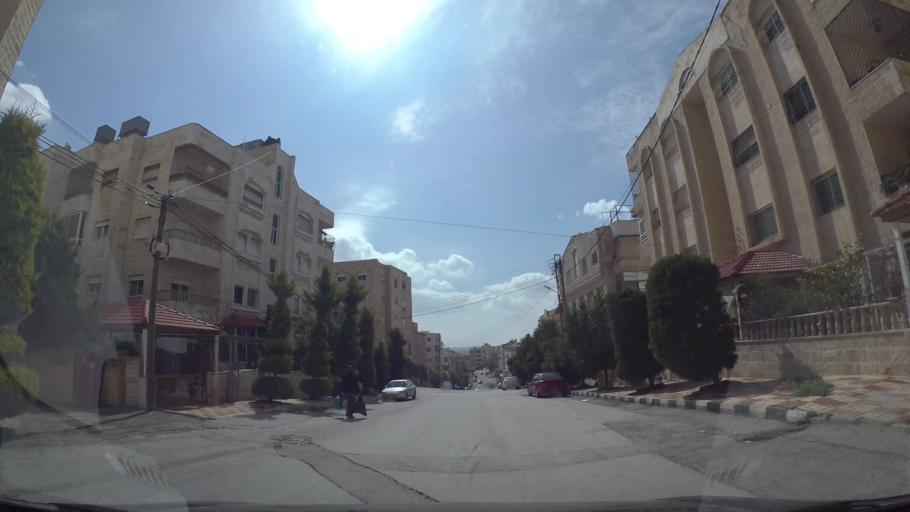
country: JO
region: Amman
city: Al Jubayhah
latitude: 31.9968
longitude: 35.9070
